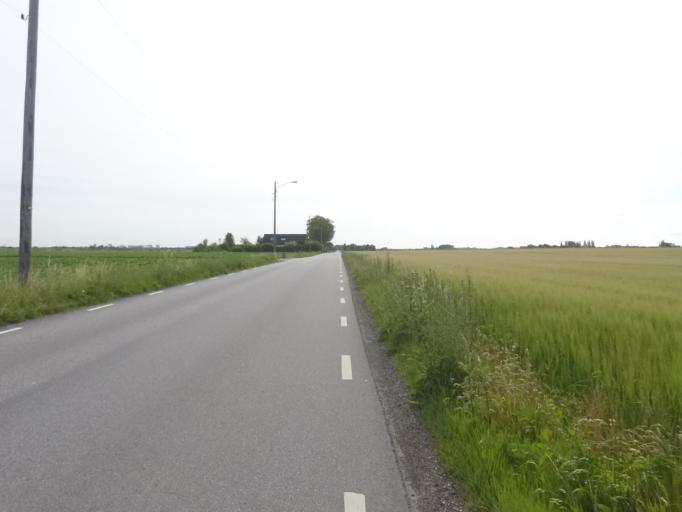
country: SE
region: Skane
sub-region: Malmo
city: Bunkeflostrand
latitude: 55.5438
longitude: 12.9466
